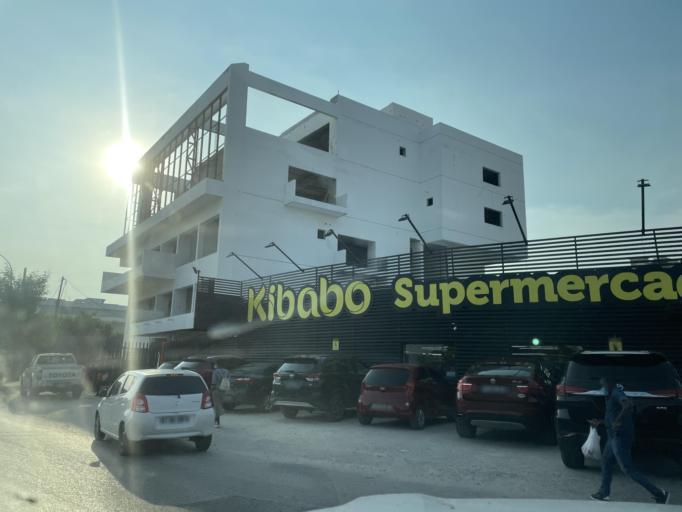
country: AO
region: Luanda
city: Luanda
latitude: -8.9227
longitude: 13.1959
